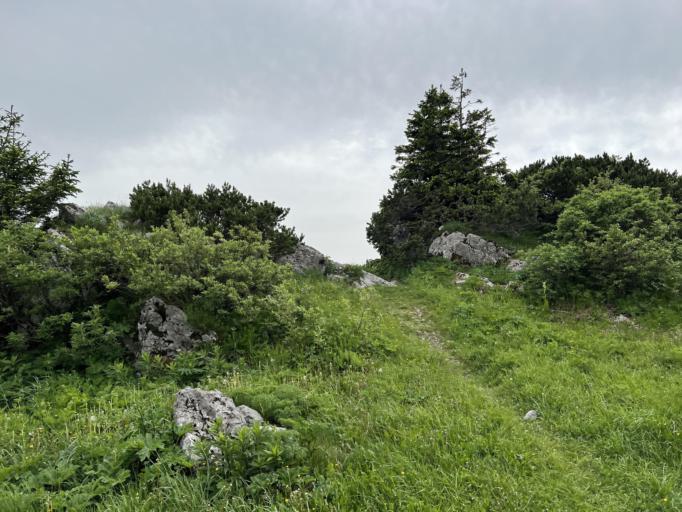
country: SI
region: Osilnica
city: Osilnica
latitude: 45.4293
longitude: 14.6220
